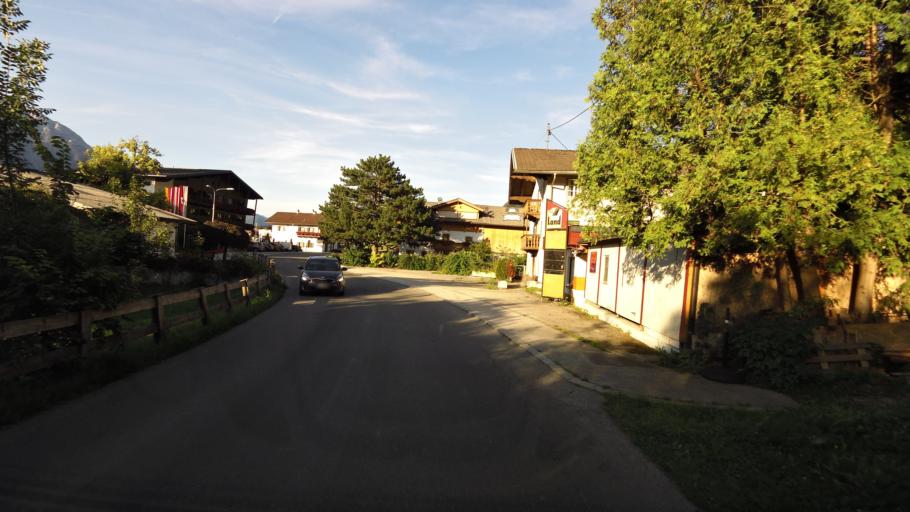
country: AT
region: Tyrol
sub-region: Politischer Bezirk Schwaz
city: Gallzein
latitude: 47.3770
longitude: 11.7676
